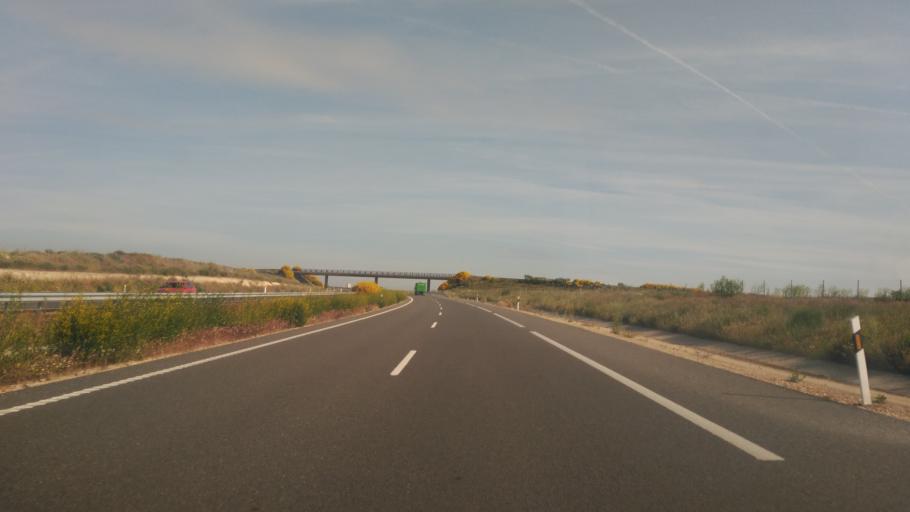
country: ES
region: Castille and Leon
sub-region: Provincia de Salamanca
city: Castellanos de Villiquera
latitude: 41.0482
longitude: -5.6685
